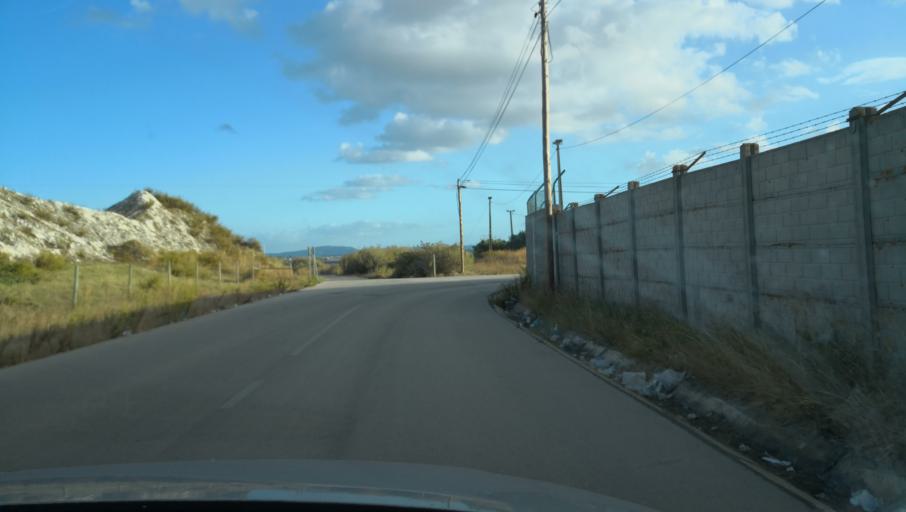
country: PT
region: Setubal
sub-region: Moita
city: Alhos Vedros
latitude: 38.6721
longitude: -9.0449
